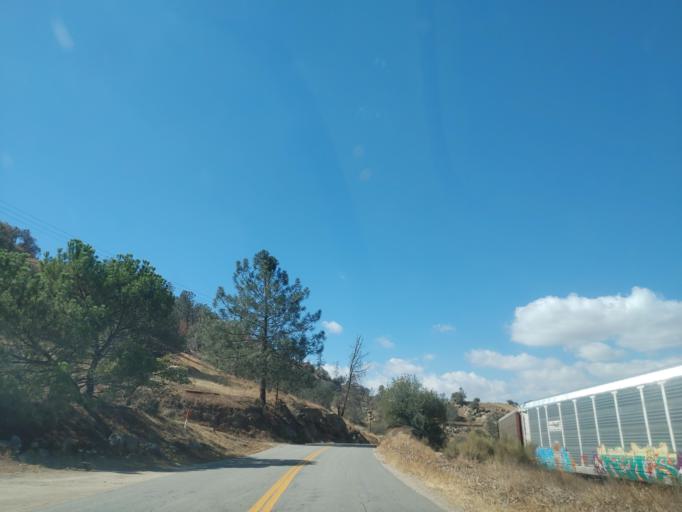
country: US
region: California
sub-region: Kern County
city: Bear Valley Springs
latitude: 35.2177
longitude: -118.5567
